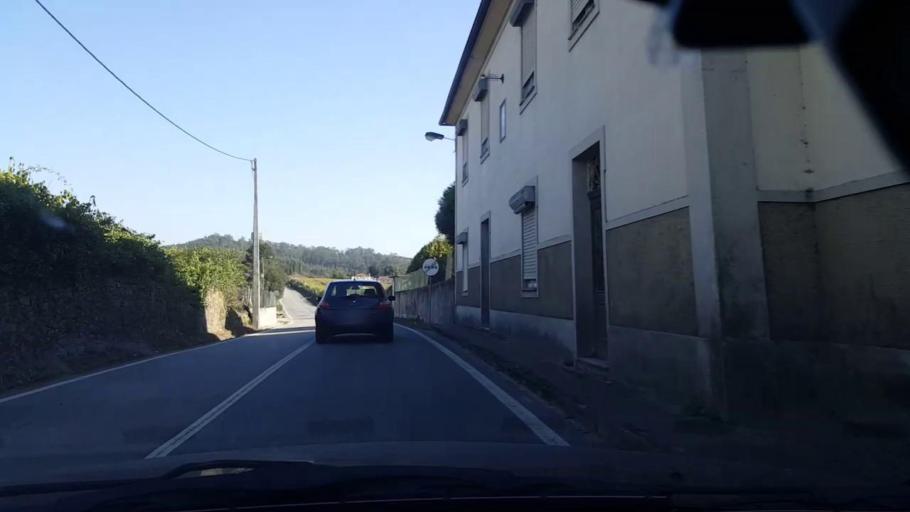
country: PT
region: Porto
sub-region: Vila do Conde
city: Arvore
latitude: 41.3305
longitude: -8.6619
